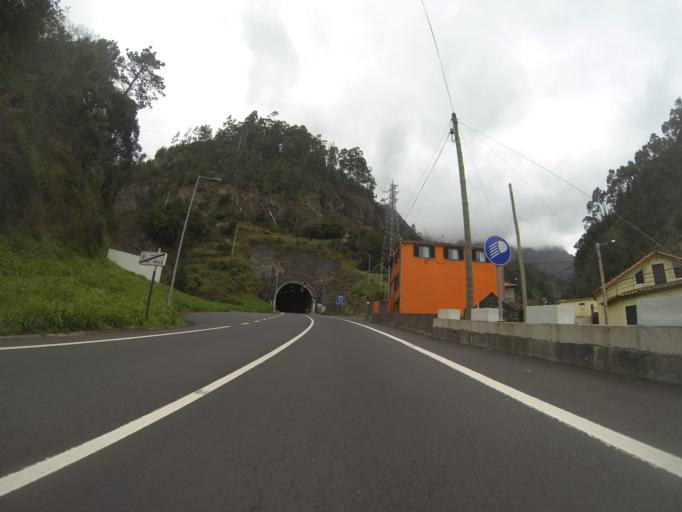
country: PT
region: Madeira
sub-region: Camara de Lobos
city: Curral das Freiras
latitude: 32.7412
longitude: -17.0177
